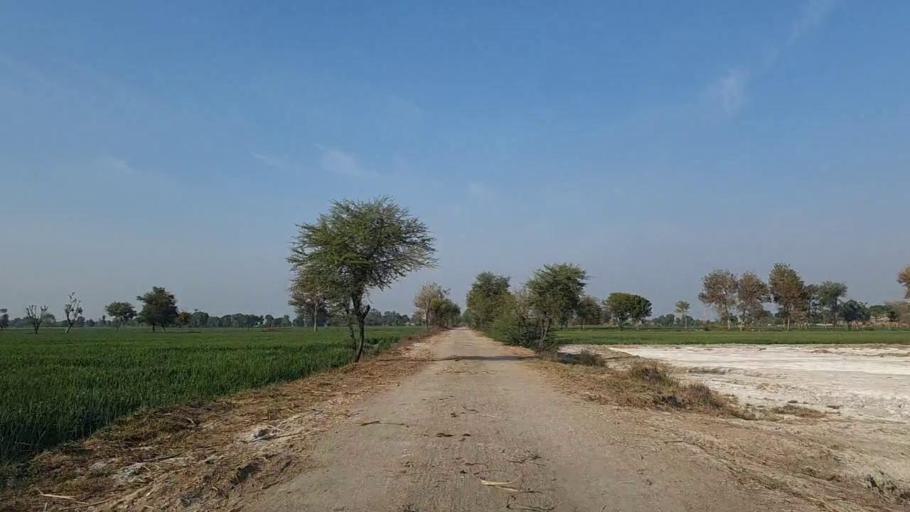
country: PK
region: Sindh
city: Nawabshah
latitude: 26.3763
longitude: 68.4850
